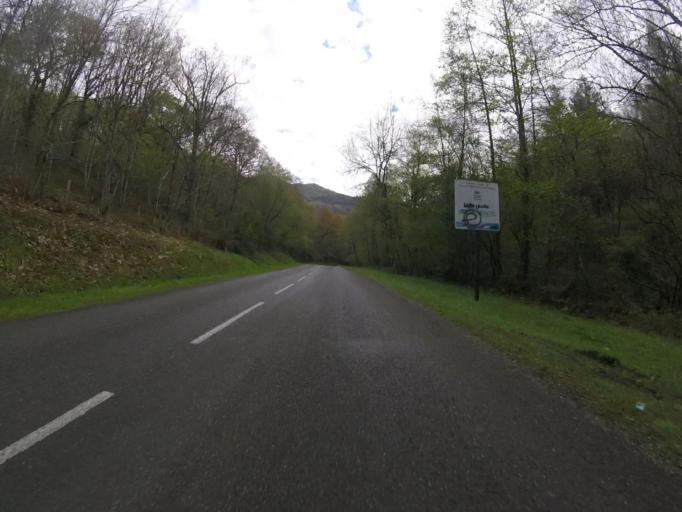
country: ES
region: Navarre
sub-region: Provincia de Navarra
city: Etxalar
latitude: 43.2836
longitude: -1.6268
